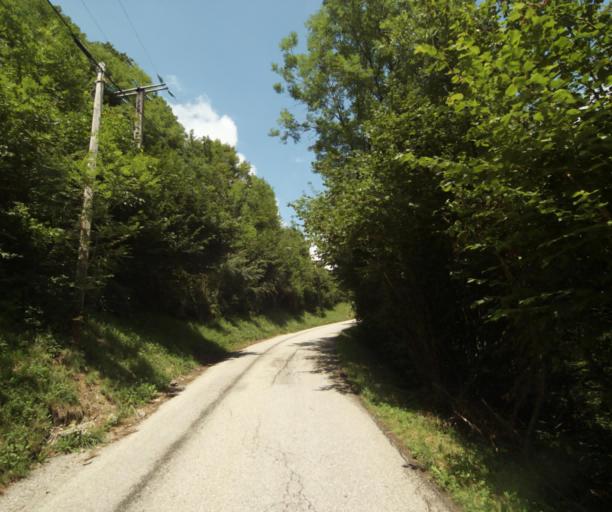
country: FR
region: Rhone-Alpes
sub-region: Departement de la Haute-Savoie
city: Thones
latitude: 45.9003
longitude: 6.3028
